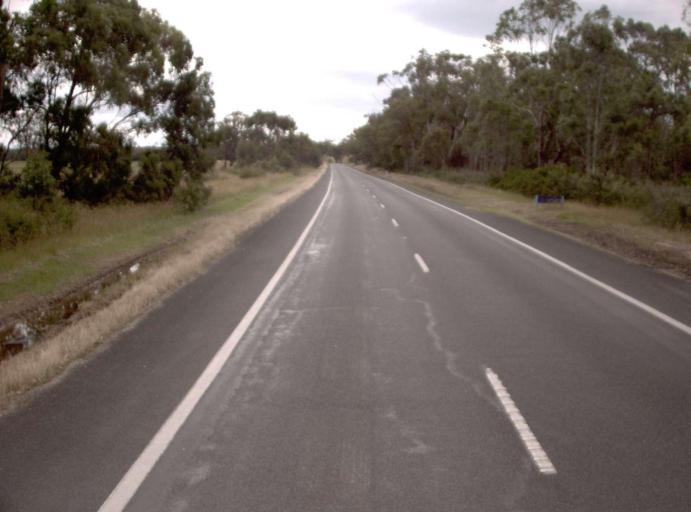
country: AU
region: Victoria
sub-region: Wellington
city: Sale
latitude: -38.2807
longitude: 147.0371
